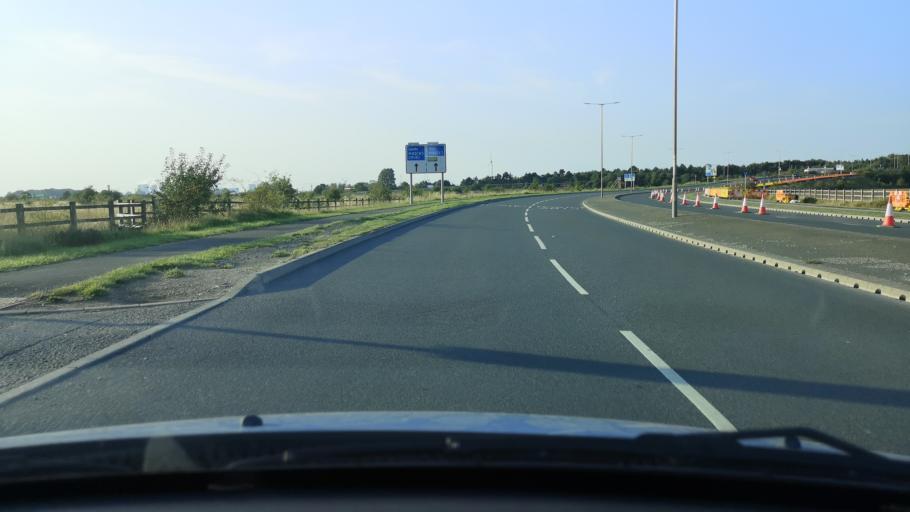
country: GB
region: England
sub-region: East Riding of Yorkshire
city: Airmyn
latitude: 53.7014
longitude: -0.9083
